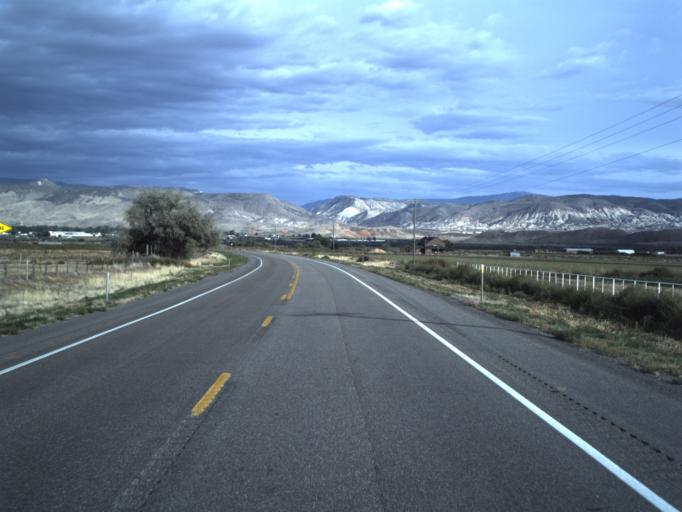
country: US
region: Utah
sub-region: Sevier County
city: Aurora
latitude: 38.9559
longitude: -111.9172
